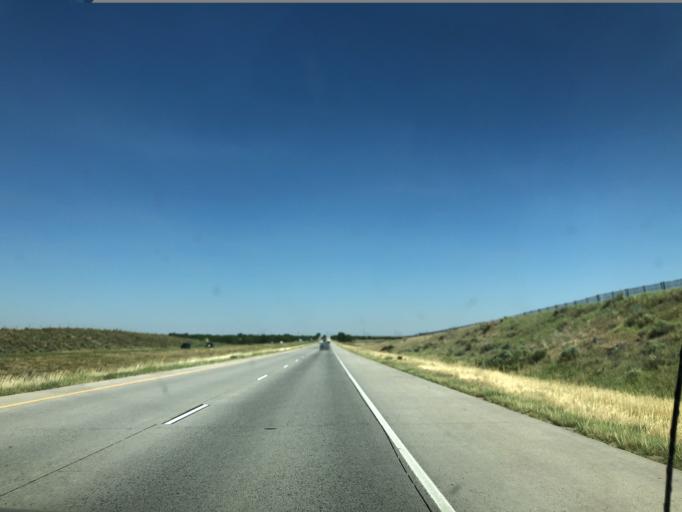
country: US
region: Colorado
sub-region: Arapahoe County
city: Byers
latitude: 39.6387
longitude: -104.0596
